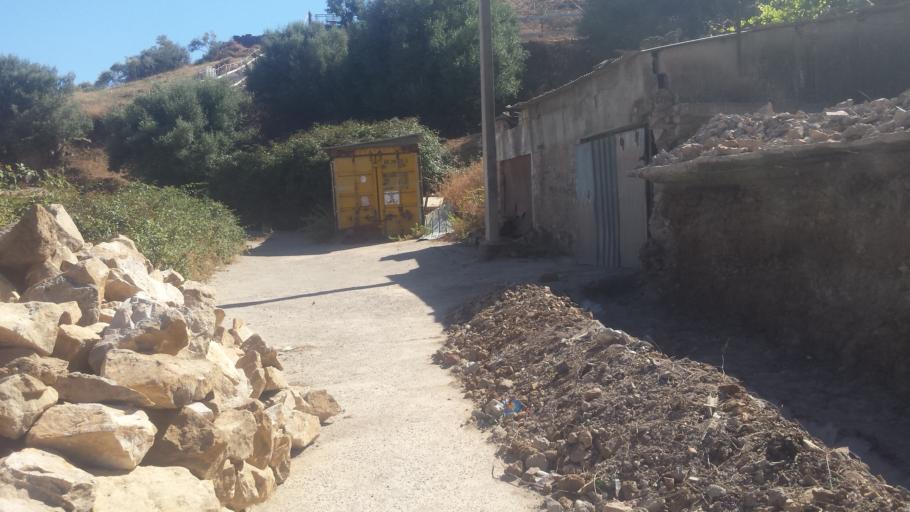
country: DZ
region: Tizi Ouzou
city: Chemini
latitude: 36.6056
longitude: 4.6379
